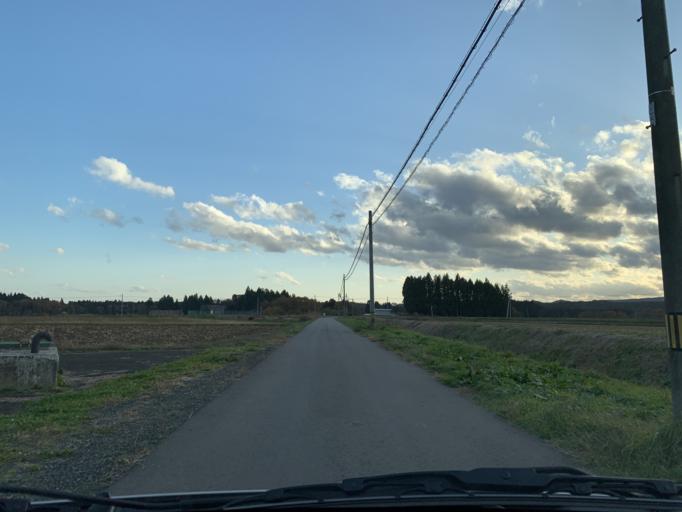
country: JP
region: Iwate
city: Mizusawa
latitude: 39.0896
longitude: 141.0369
